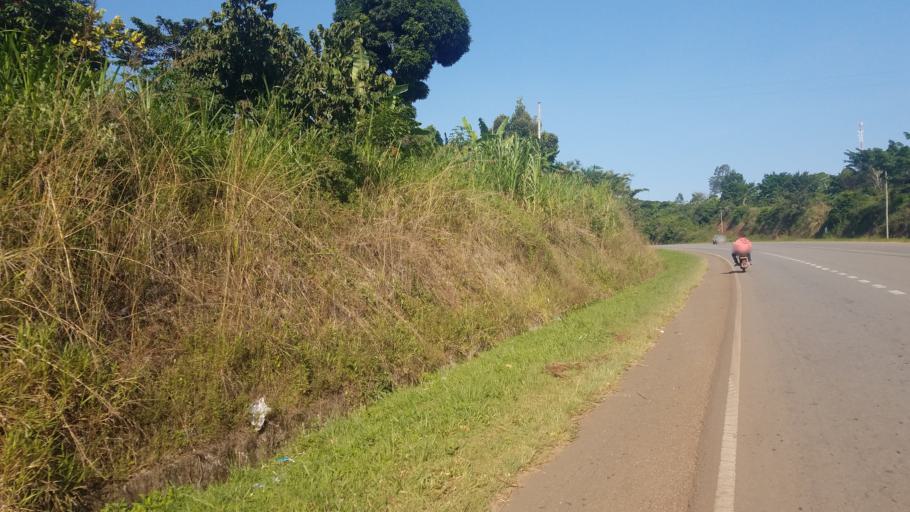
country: UG
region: Central Region
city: Masaka
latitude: -0.3375
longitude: 31.6825
